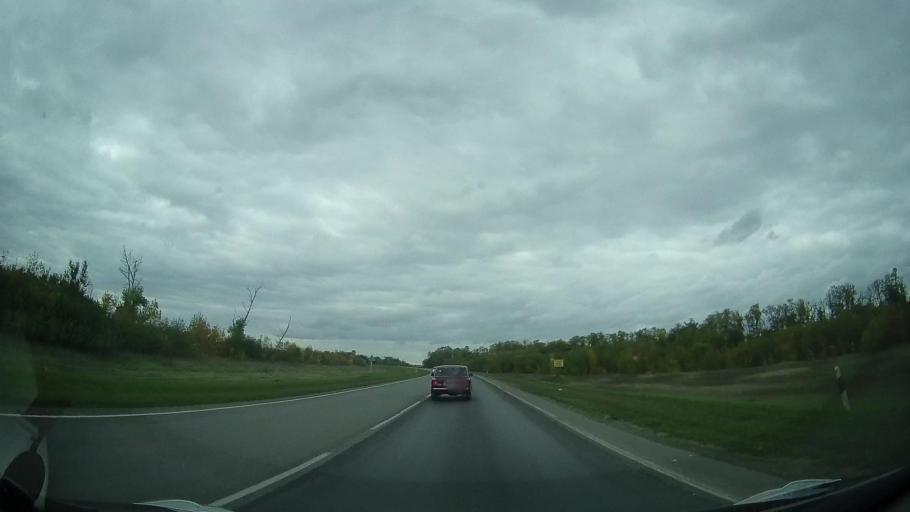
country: RU
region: Rostov
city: Yegorlykskaya
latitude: 46.5448
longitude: 40.7670
